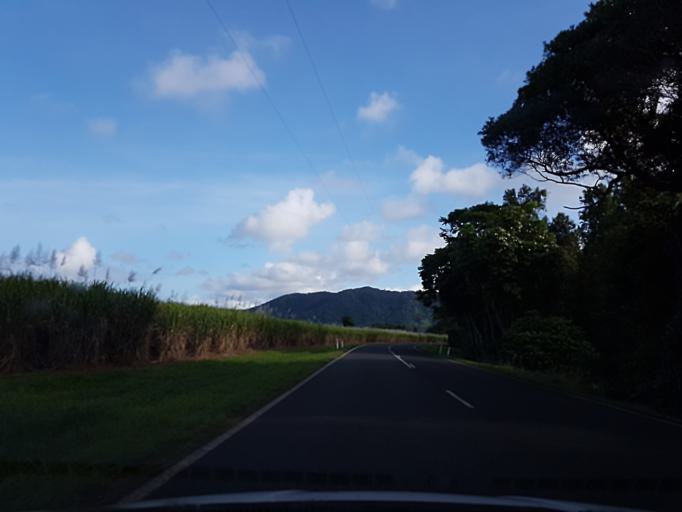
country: AU
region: Queensland
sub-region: Cairns
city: Port Douglas
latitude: -16.2737
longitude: 145.3908
